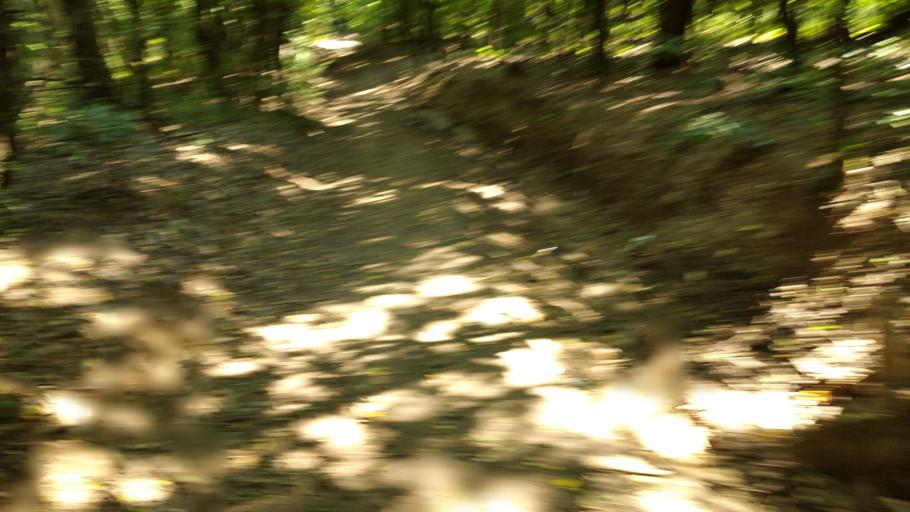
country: HU
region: Nograd
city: Nagyoroszi
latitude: 48.0249
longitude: 19.0425
